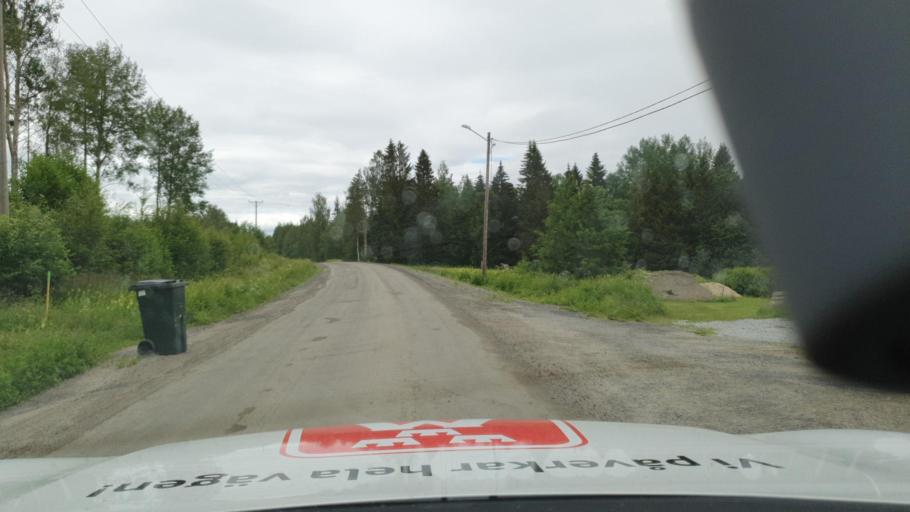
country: SE
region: Vaesterbotten
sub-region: Nordmalings Kommun
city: Nordmaling
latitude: 63.6489
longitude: 19.4345
